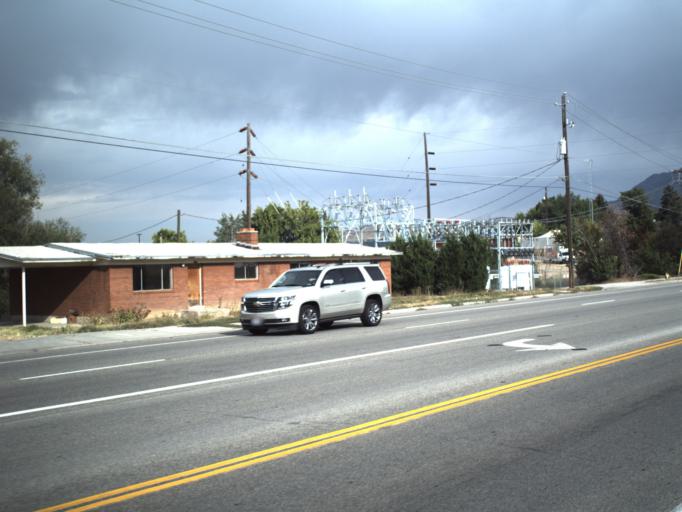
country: US
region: Utah
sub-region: Weber County
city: North Ogden
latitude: 41.2966
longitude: -111.9688
